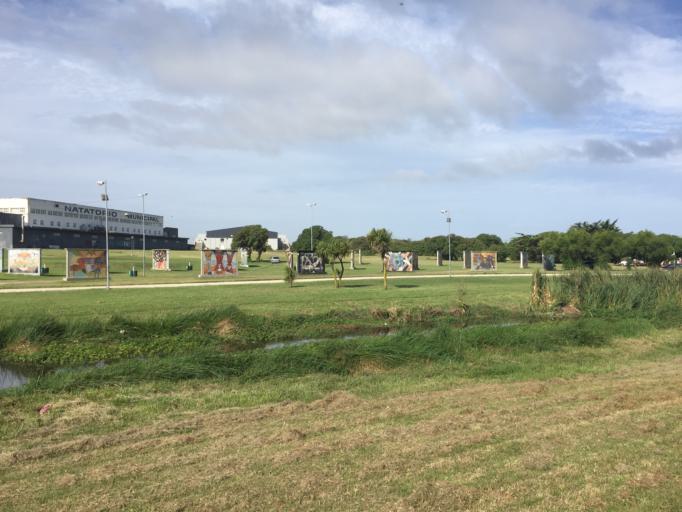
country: AR
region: Buenos Aires
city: Miramar
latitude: -38.2689
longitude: -57.8284
